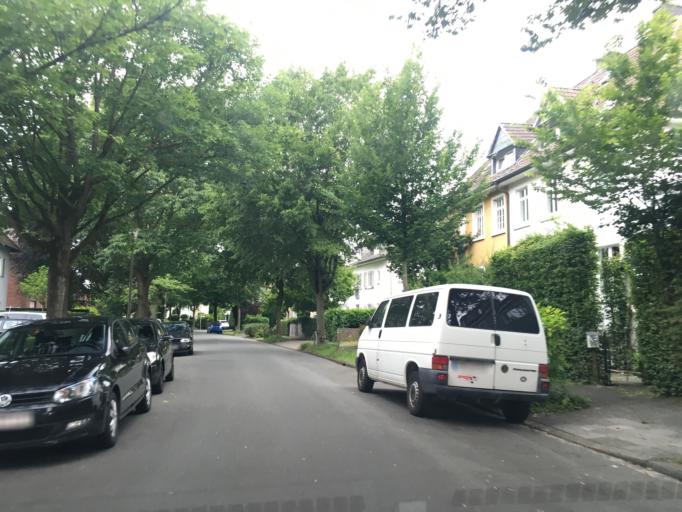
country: DE
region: North Rhine-Westphalia
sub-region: Regierungsbezirk Munster
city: Muenster
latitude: 51.9367
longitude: 7.6197
